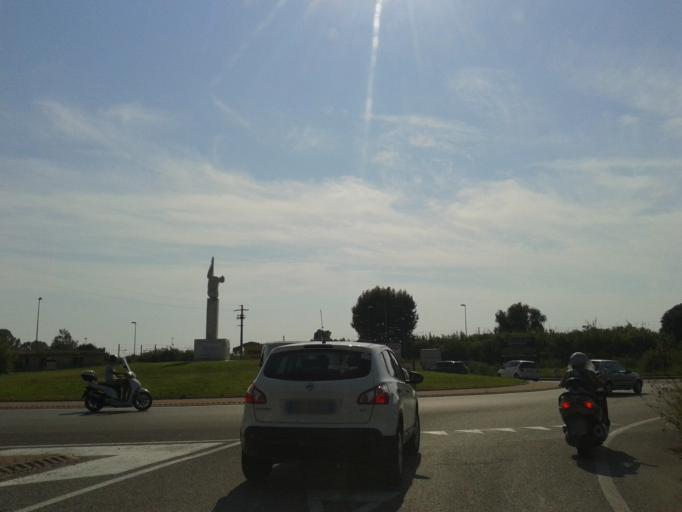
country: IT
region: Tuscany
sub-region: Provincia di Lucca
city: Camaiore
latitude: 43.8945
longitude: 10.2519
